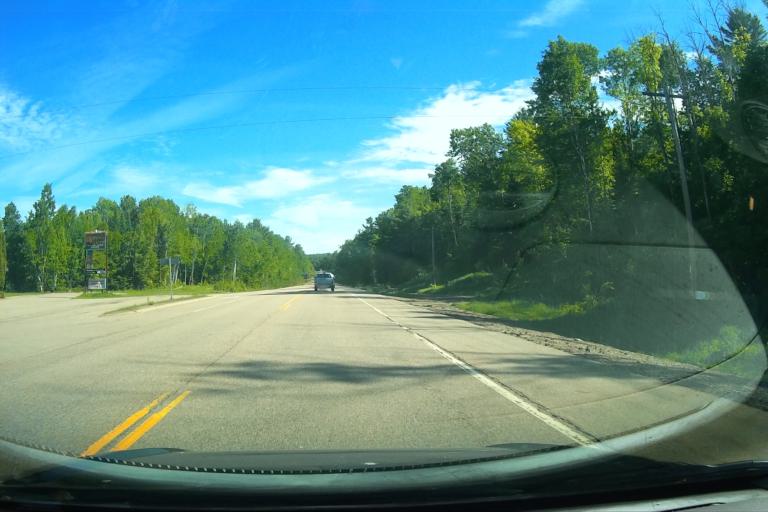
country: CA
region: Ontario
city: Deep River
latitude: 46.1988
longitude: -77.8812
